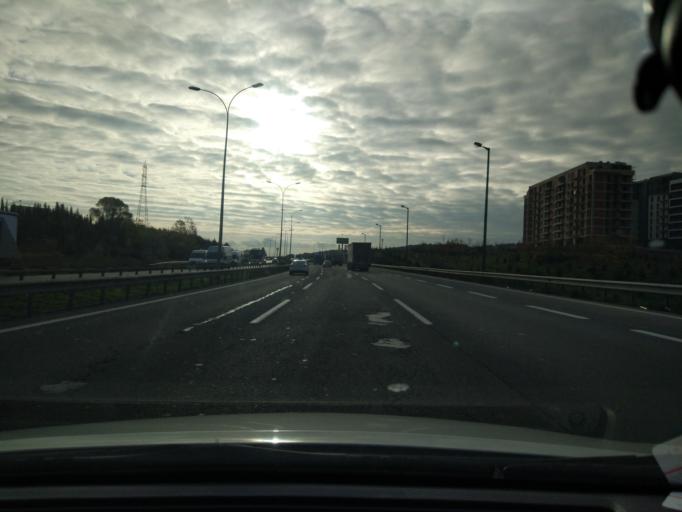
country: TR
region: Kocaeli
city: Balcik
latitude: 40.8388
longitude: 29.4166
